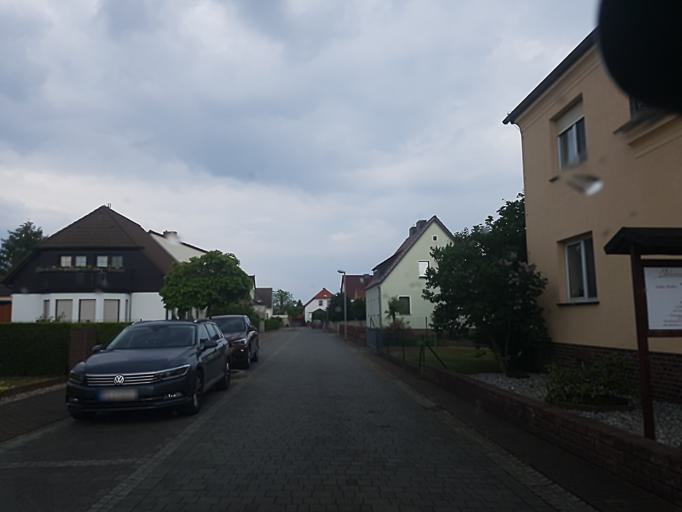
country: DE
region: Saxony-Anhalt
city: Elster
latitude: 51.8298
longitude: 12.8304
